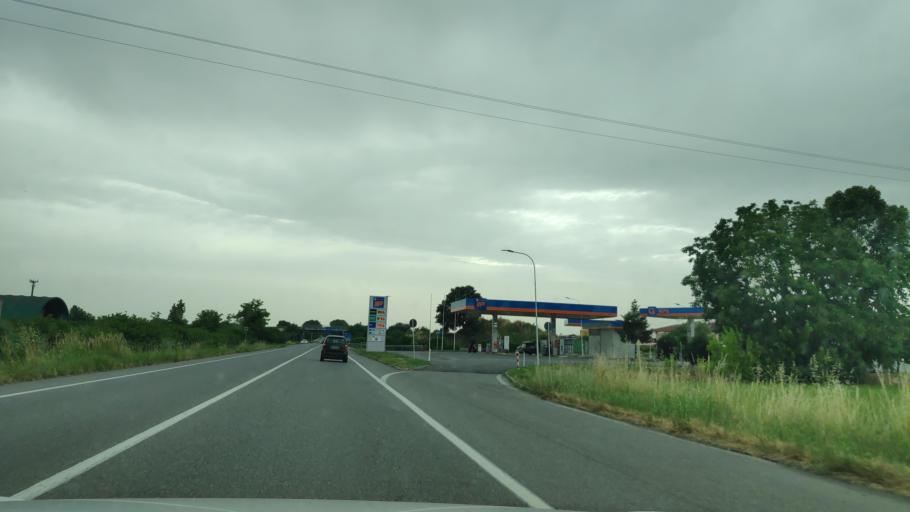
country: IT
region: Lombardy
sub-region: Provincia di Cremona
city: Soncino
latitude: 45.4105
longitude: 9.8704
